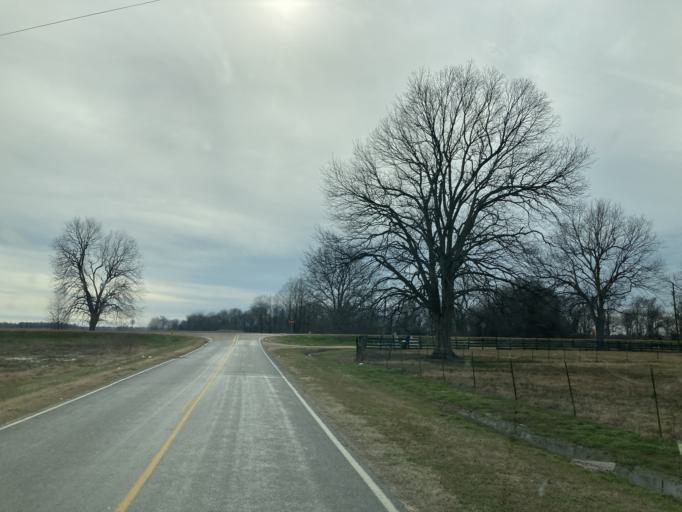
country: US
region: Mississippi
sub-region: Washington County
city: Hollandale
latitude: 33.1854
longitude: -90.6823
